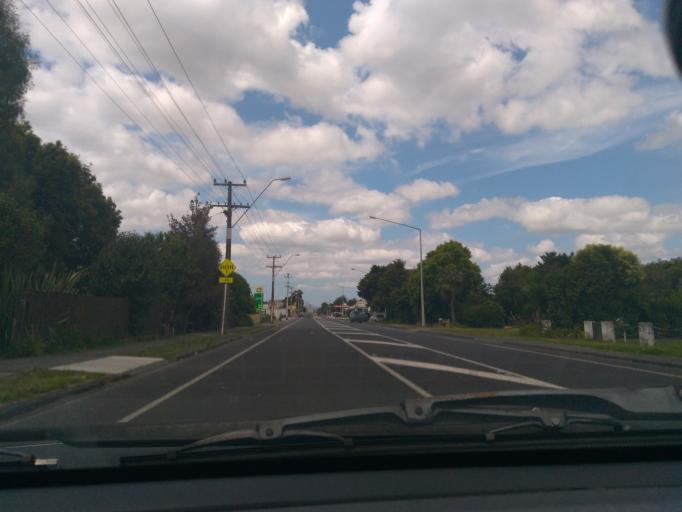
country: NZ
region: Northland
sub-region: Far North District
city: Moerewa
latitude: -35.3885
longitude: 174.0121
